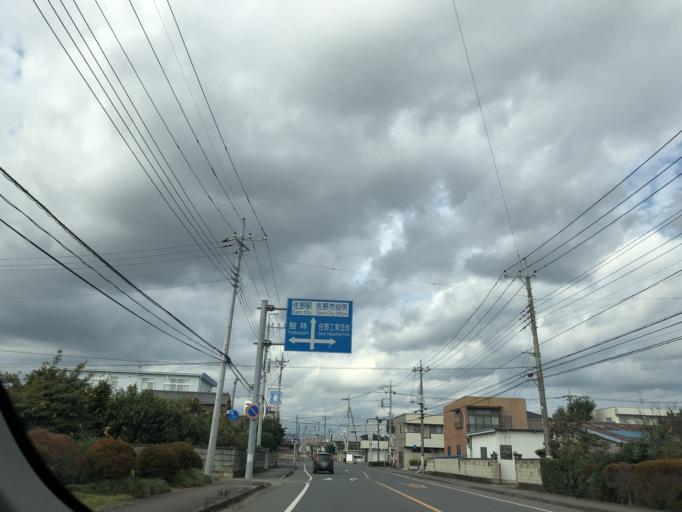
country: JP
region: Tochigi
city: Sano
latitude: 36.3032
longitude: 139.5788
